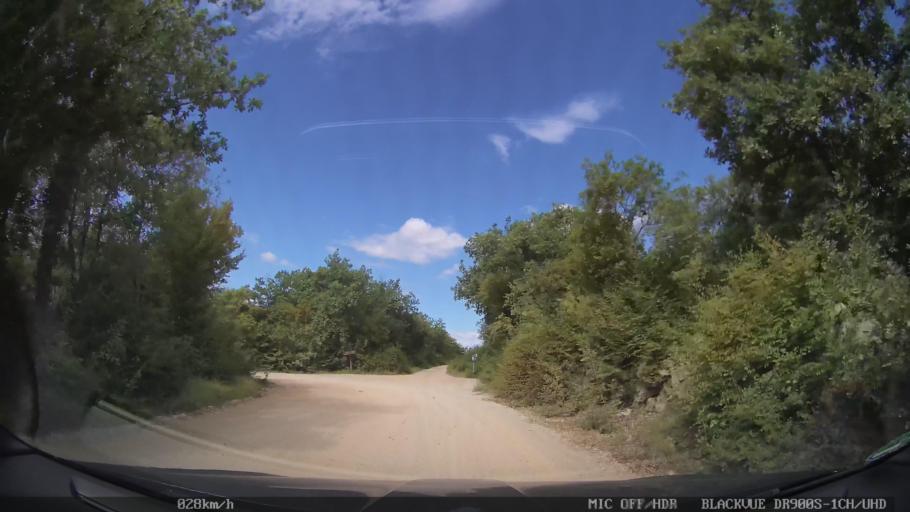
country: HR
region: Primorsko-Goranska
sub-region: Grad Krk
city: Krk
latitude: 45.0368
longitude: 14.5293
